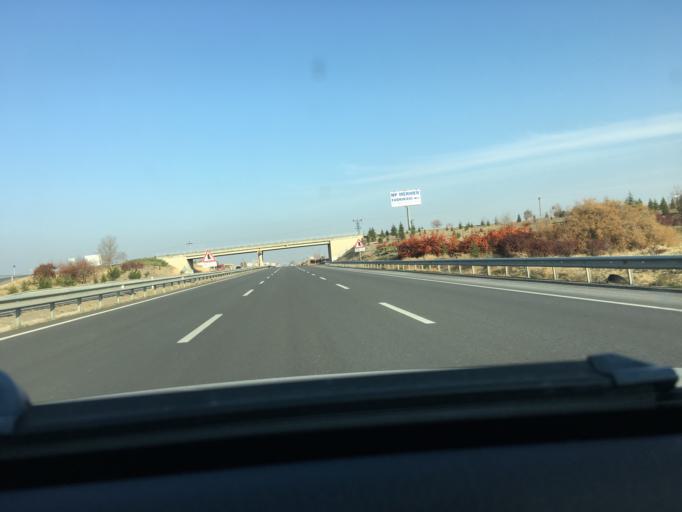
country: TR
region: Ankara
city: Temelli
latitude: 39.7189
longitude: 32.3239
